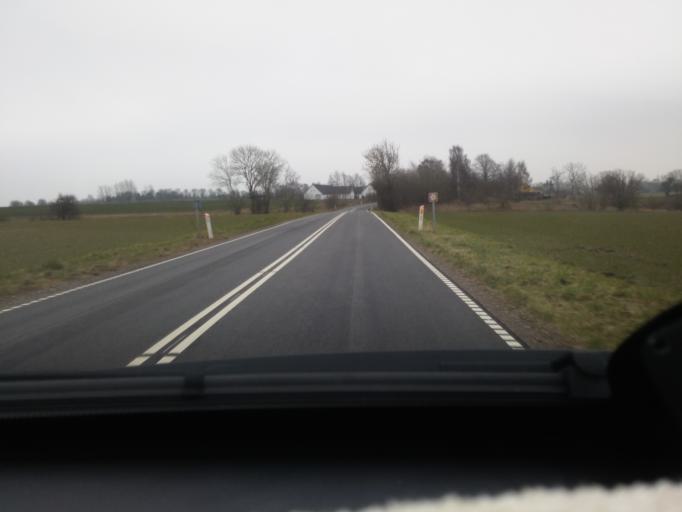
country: DK
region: South Denmark
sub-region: Kerteminde Kommune
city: Kerteminde
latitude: 55.4047
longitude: 10.7260
